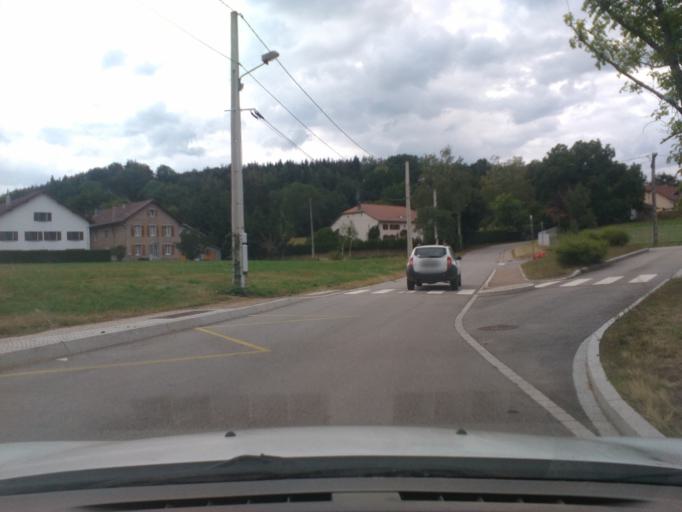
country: FR
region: Lorraine
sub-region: Departement des Vosges
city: Saint-Michel-sur-Meurthe
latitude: 48.3091
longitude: 6.8721
